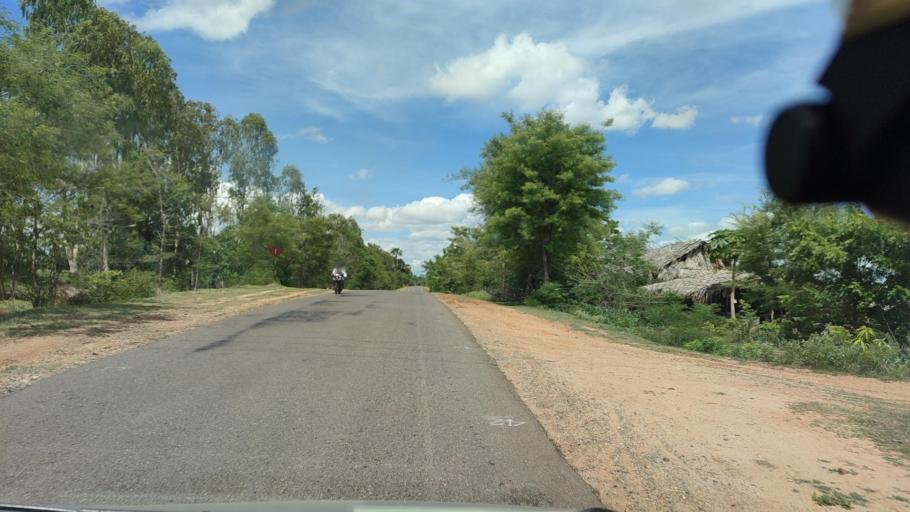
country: MM
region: Magway
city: Magway
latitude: 20.1920
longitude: 95.1496
